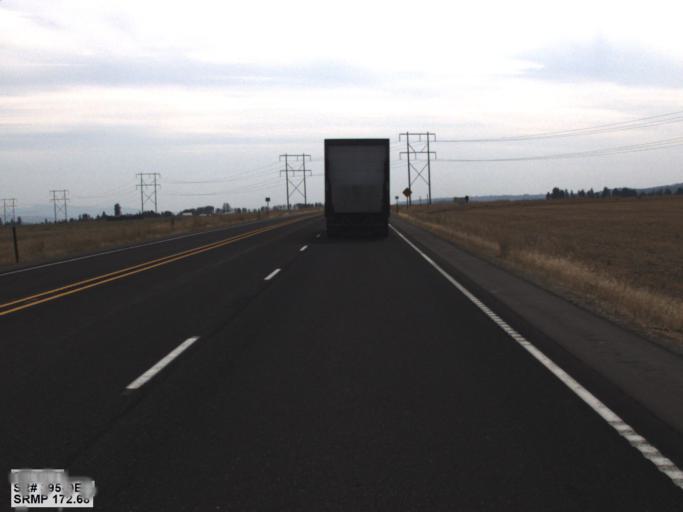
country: US
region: Washington
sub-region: Spokane County
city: Fairwood
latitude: 47.8542
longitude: -117.4219
